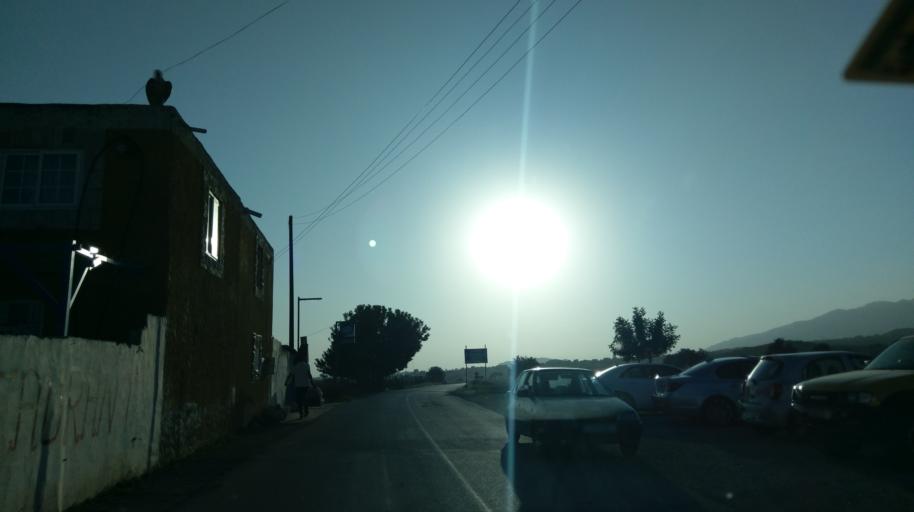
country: CY
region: Ammochostos
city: Trikomo
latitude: 35.3911
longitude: 33.9701
